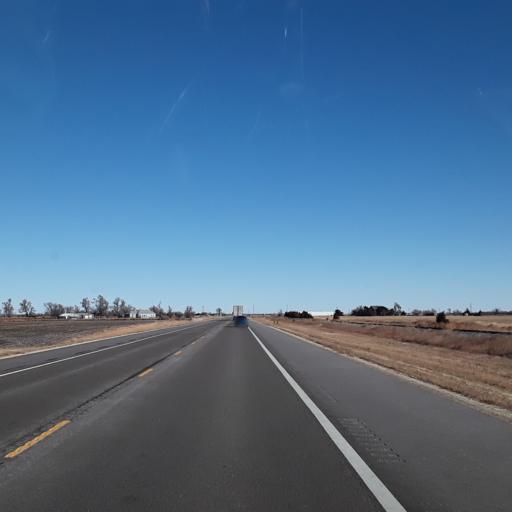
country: US
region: Kansas
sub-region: Pawnee County
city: Larned
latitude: 38.1961
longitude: -99.0750
